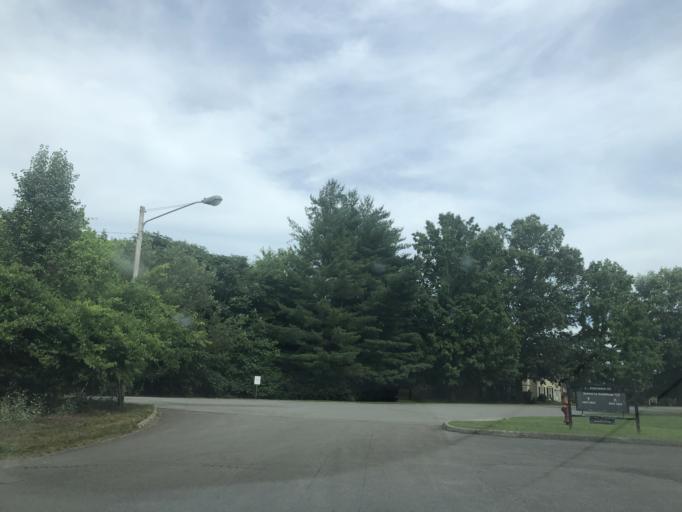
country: US
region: Tennessee
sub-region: Davidson County
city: Belle Meade
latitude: 36.0748
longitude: -86.9519
